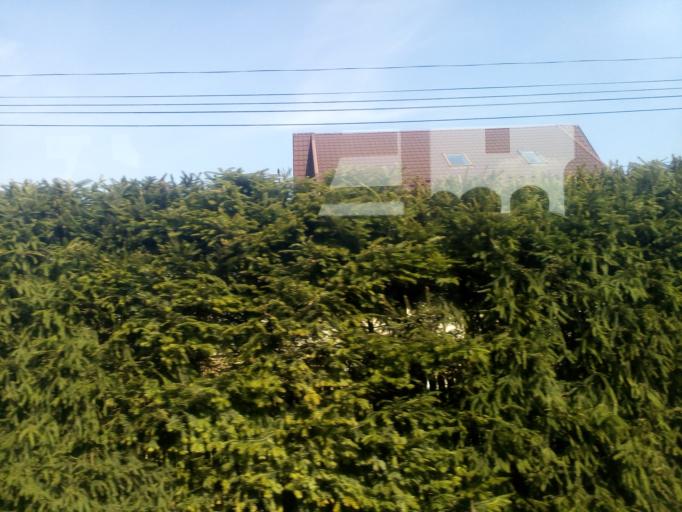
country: PL
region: Lesser Poland Voivodeship
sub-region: Powiat nowosadecki
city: Stary Sacz
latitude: 49.5664
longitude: 20.6522
